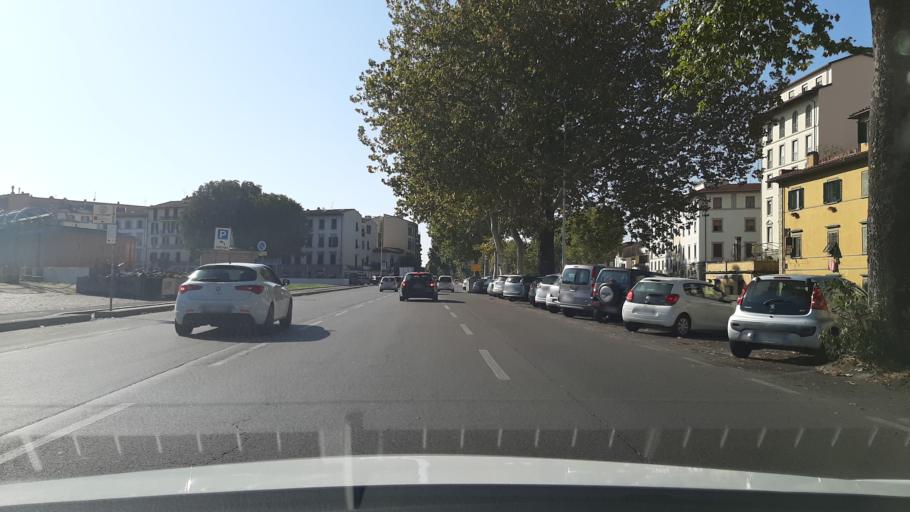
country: IT
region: Tuscany
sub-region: Province of Florence
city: Florence
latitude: 43.7864
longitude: 11.2639
